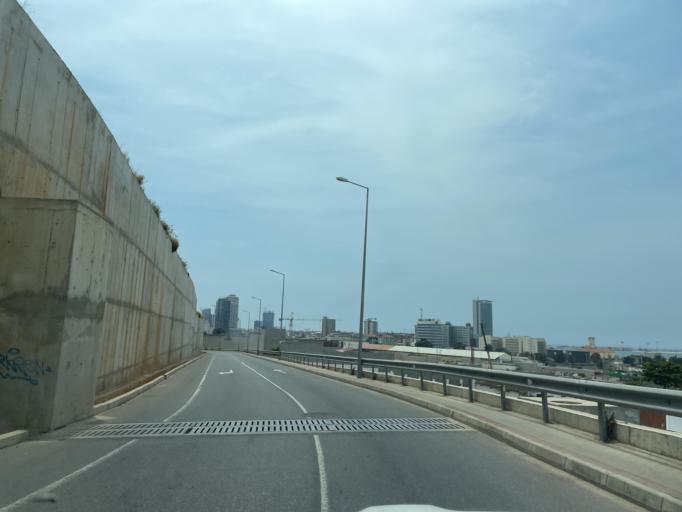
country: AO
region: Luanda
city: Luanda
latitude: -8.8047
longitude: 13.2503
